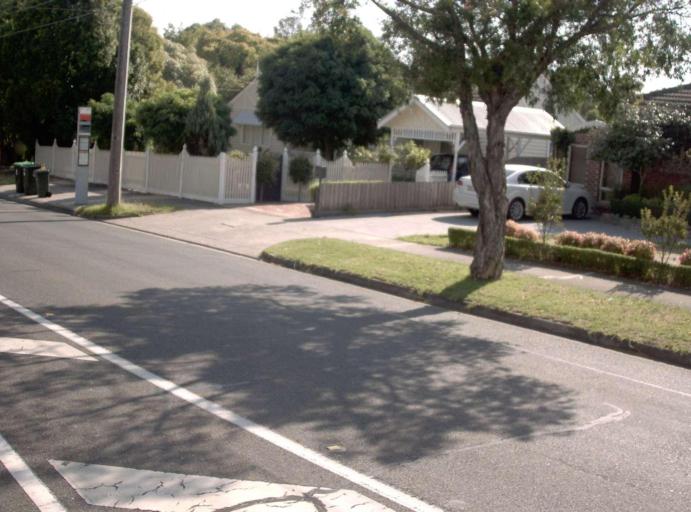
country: AU
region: Victoria
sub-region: Whitehorse
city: Box Hill North
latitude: -37.8066
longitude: 145.1260
